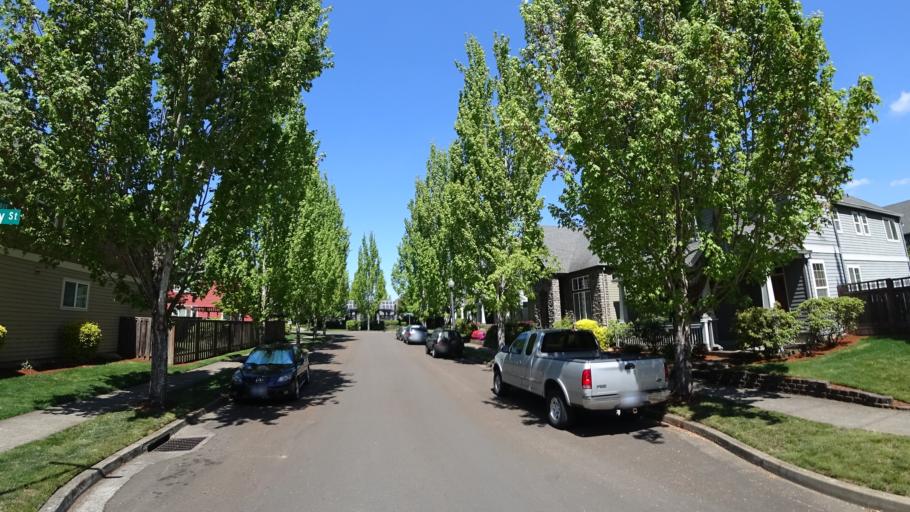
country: US
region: Oregon
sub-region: Washington County
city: Hillsboro
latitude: 45.5075
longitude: -122.9741
